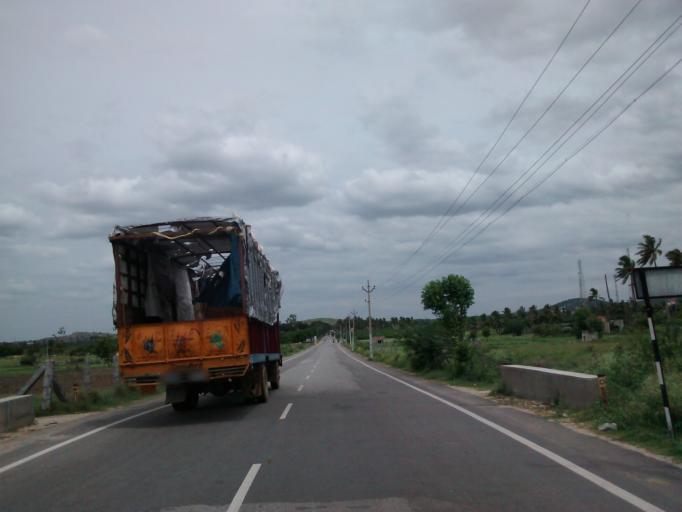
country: IN
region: Andhra Pradesh
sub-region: Chittoor
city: Chittoor
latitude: 13.2834
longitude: 79.0405
